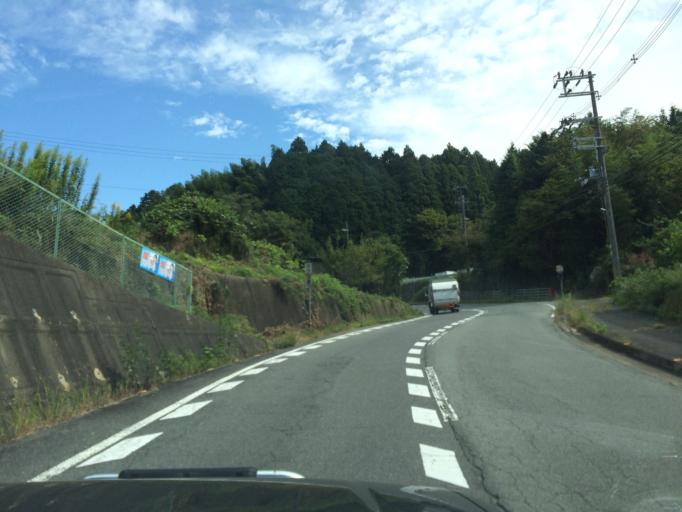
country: JP
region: Mie
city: Nabari
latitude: 34.6769
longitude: 135.9875
